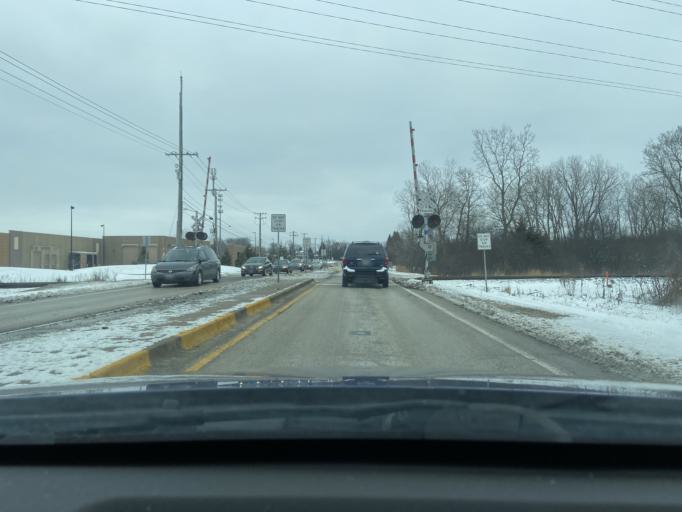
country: US
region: Illinois
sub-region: Lake County
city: Venetian Village
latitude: 42.3960
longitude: -88.0704
